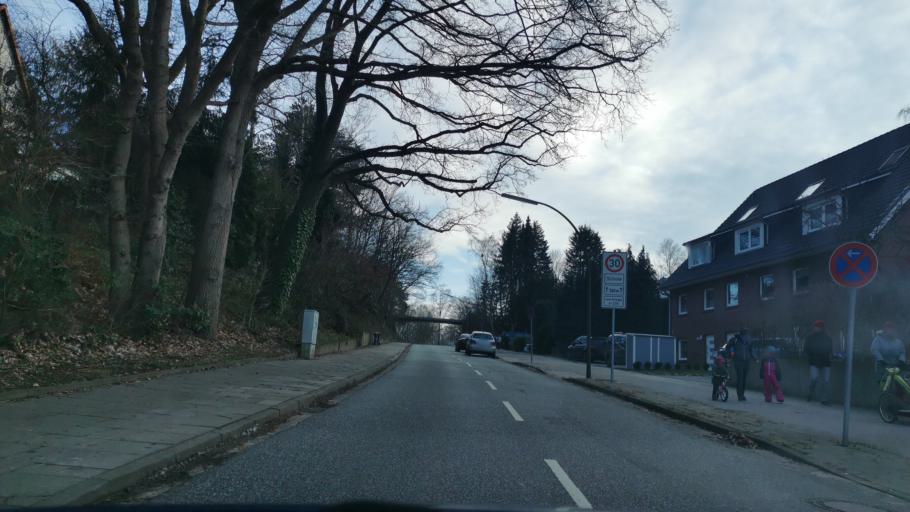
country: DE
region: Hamburg
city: Harburg
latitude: 53.4324
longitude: 9.9696
